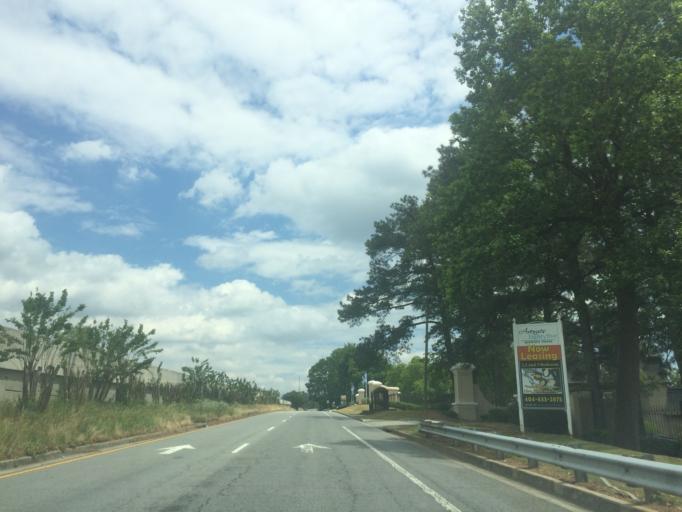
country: US
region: Georgia
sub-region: DeKalb County
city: North Druid Hills
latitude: 33.8528
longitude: -84.2988
